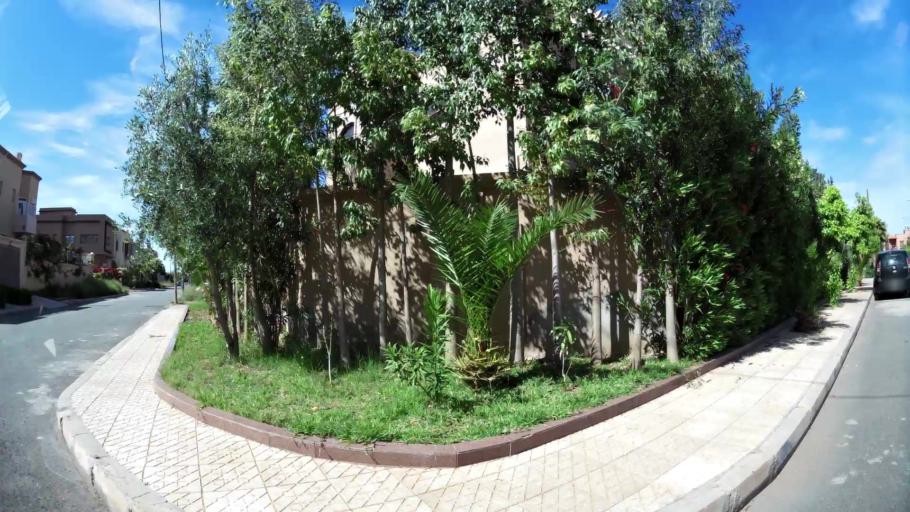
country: MA
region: Marrakech-Tensift-Al Haouz
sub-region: Marrakech
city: Marrakesh
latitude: 31.6428
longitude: -8.0445
